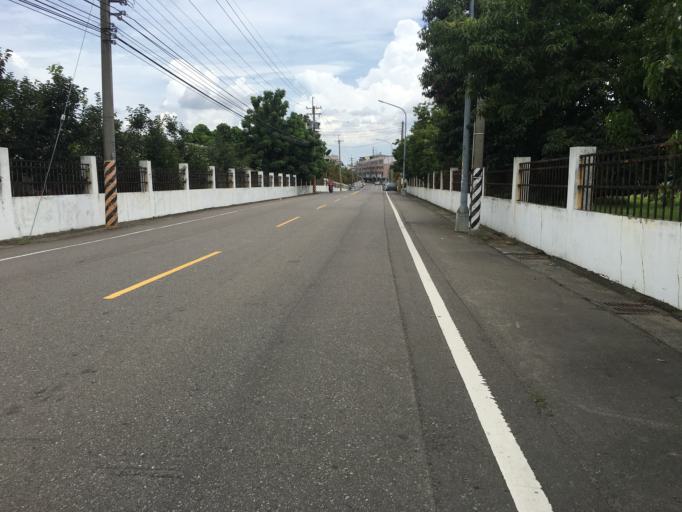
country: TW
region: Taiwan
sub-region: Taichung City
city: Taichung
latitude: 24.0772
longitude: 120.7234
